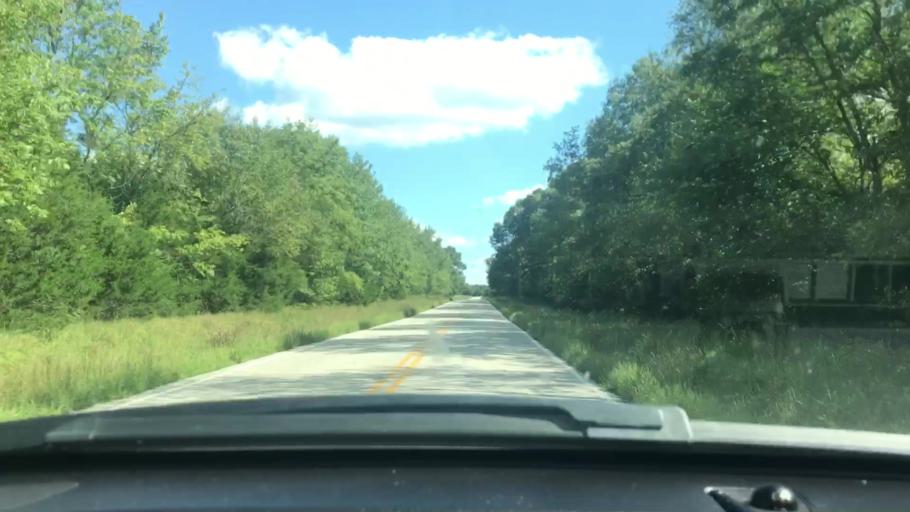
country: US
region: Missouri
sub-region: Wright County
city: Hartville
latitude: 37.3834
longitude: -92.4402
